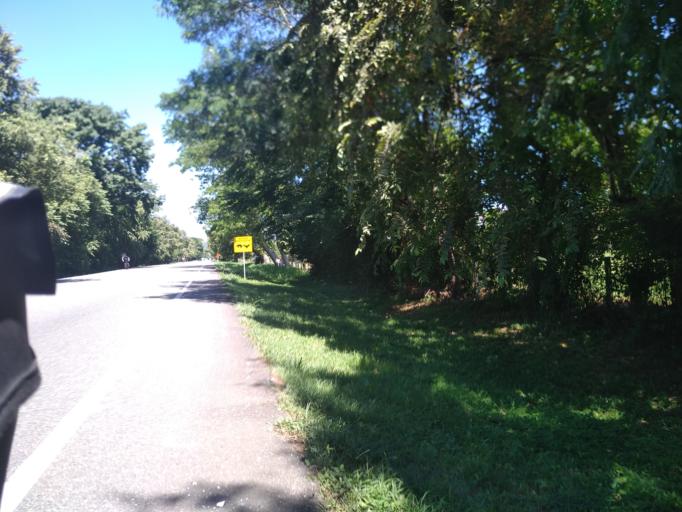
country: CO
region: Caldas
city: La Dorada
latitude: 5.3605
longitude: -74.7242
